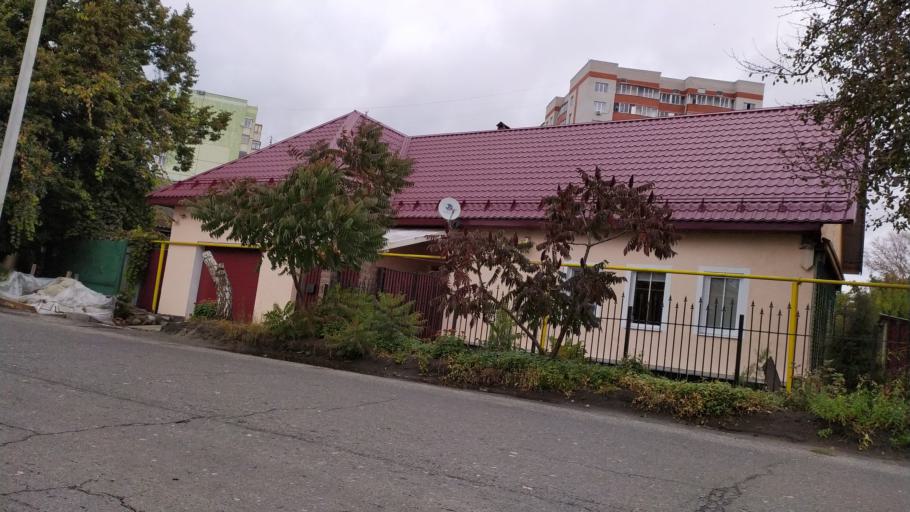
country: RU
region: Kursk
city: Kursk
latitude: 51.6473
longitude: 36.1442
